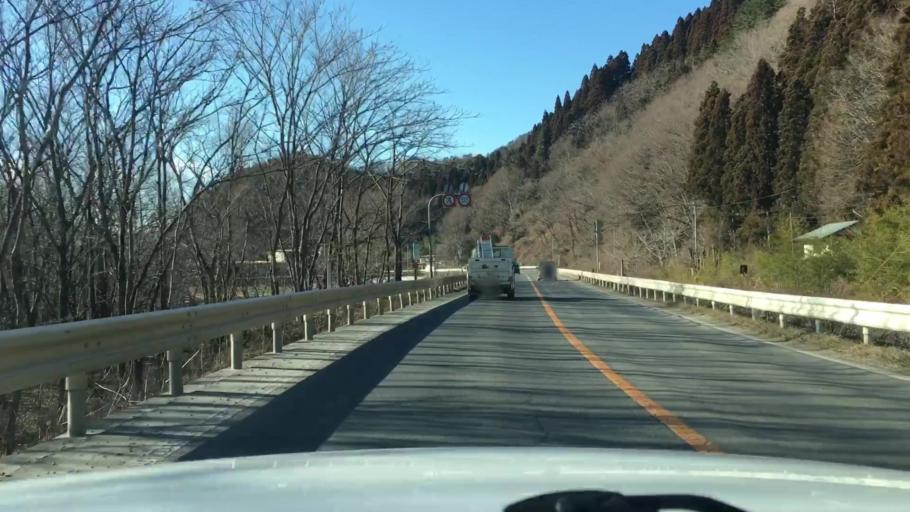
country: JP
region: Iwate
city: Miyako
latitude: 39.6323
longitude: 141.8845
